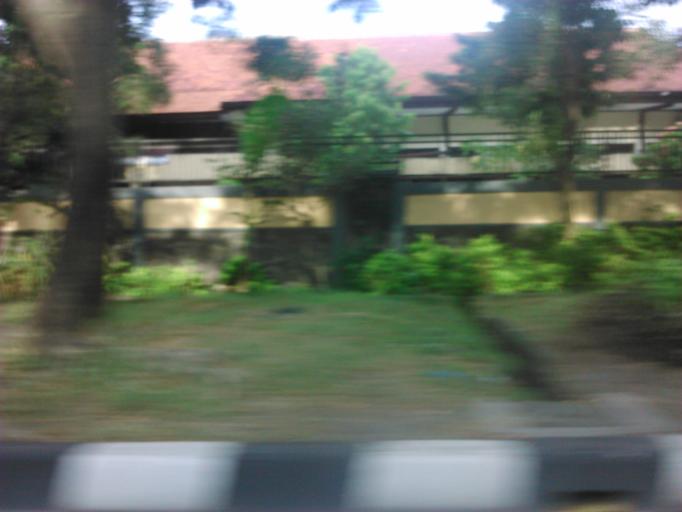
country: ID
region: East Java
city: Semampir
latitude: -7.2884
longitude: 112.7807
